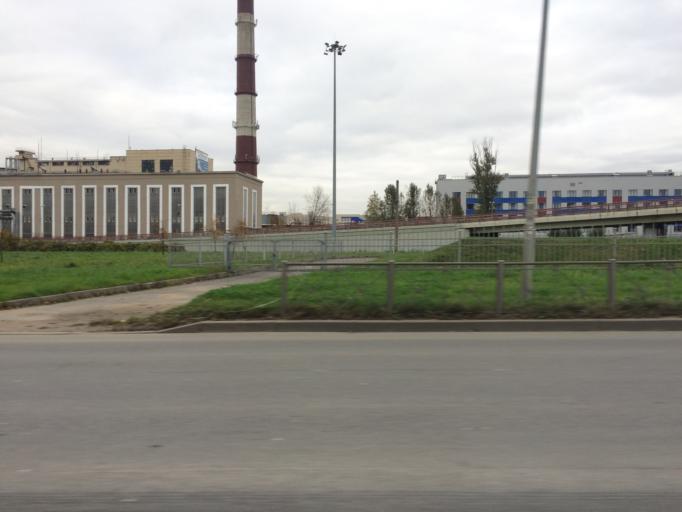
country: RU
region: Leningrad
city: Rybatskoye
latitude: 59.8562
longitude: 30.4779
